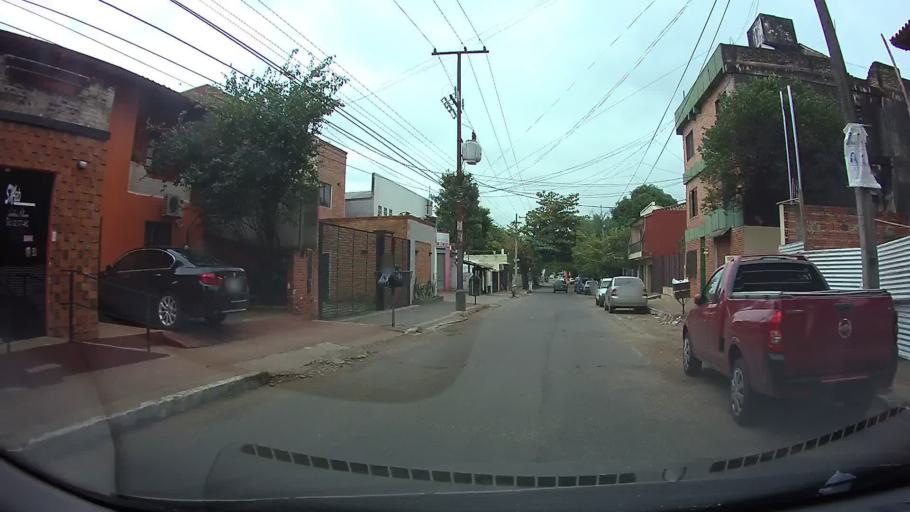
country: PY
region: Central
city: Lambare
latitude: -25.3191
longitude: -57.6081
